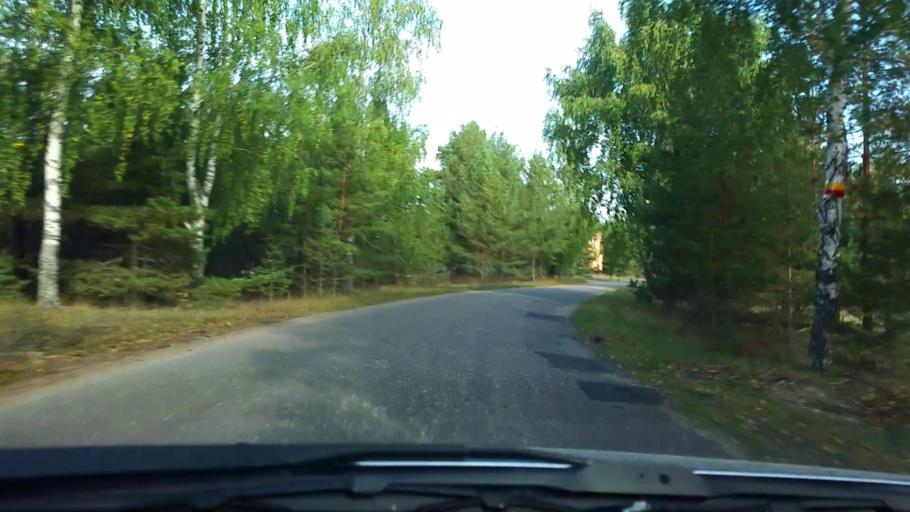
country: LV
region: Adazi
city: Adazi
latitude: 57.1143
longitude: 24.3621
